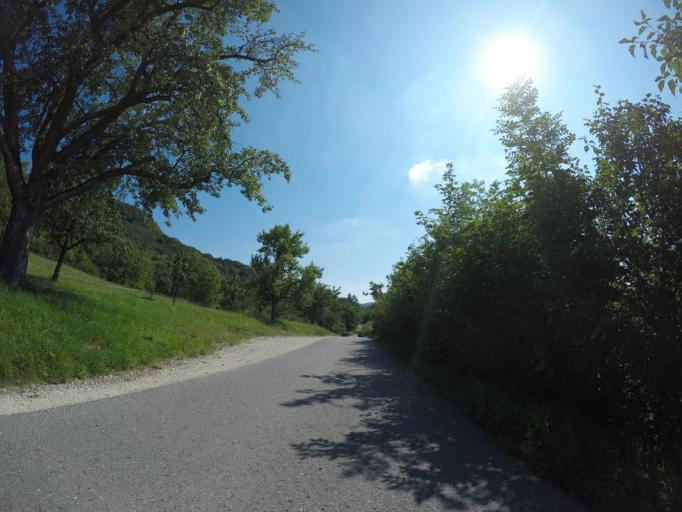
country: DE
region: Baden-Wuerttemberg
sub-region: Tuebingen Region
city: Pfullingen
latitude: 48.4636
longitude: 9.2421
